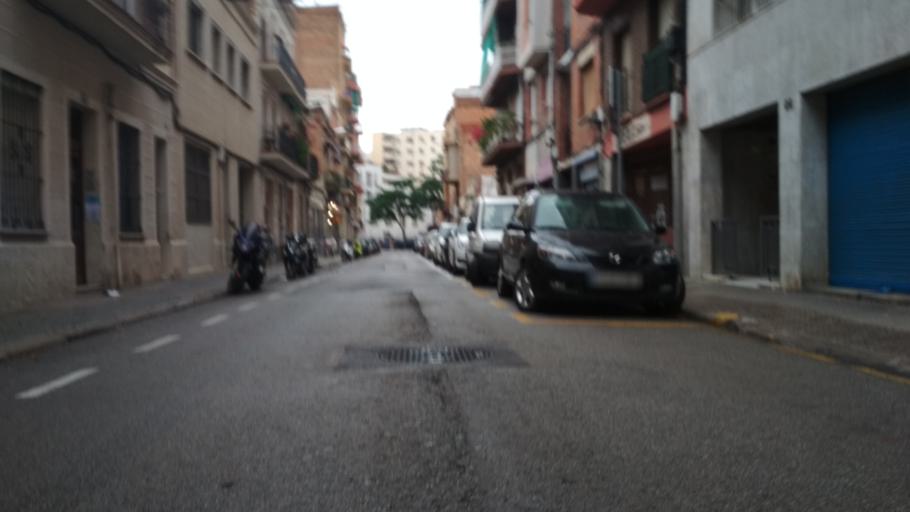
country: ES
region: Catalonia
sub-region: Provincia de Barcelona
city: Sant Marti
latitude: 41.4157
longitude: 2.1845
